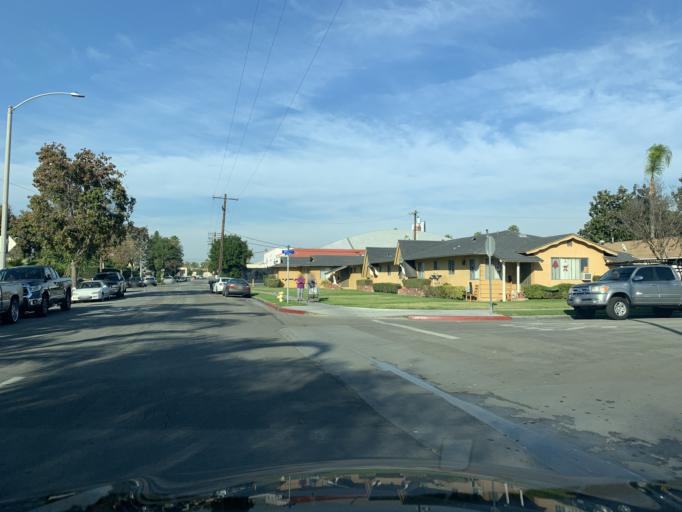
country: US
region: California
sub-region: Orange County
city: Anaheim
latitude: 33.8156
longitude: -117.9089
